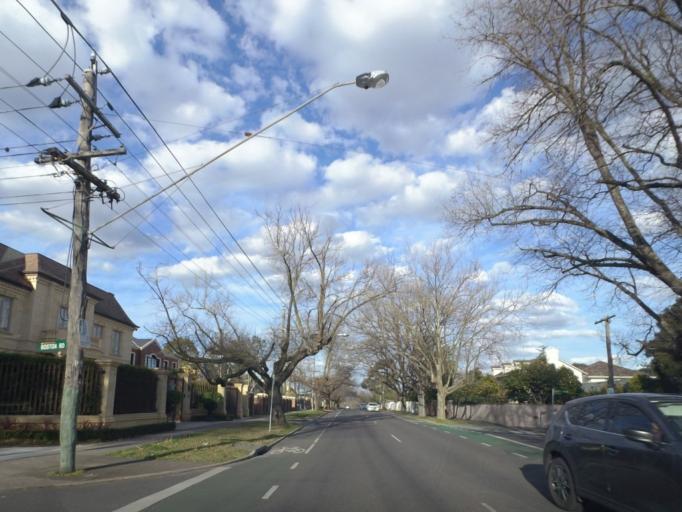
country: AU
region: Victoria
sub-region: Boroondara
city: Canterbury
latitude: -37.8179
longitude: 145.0771
